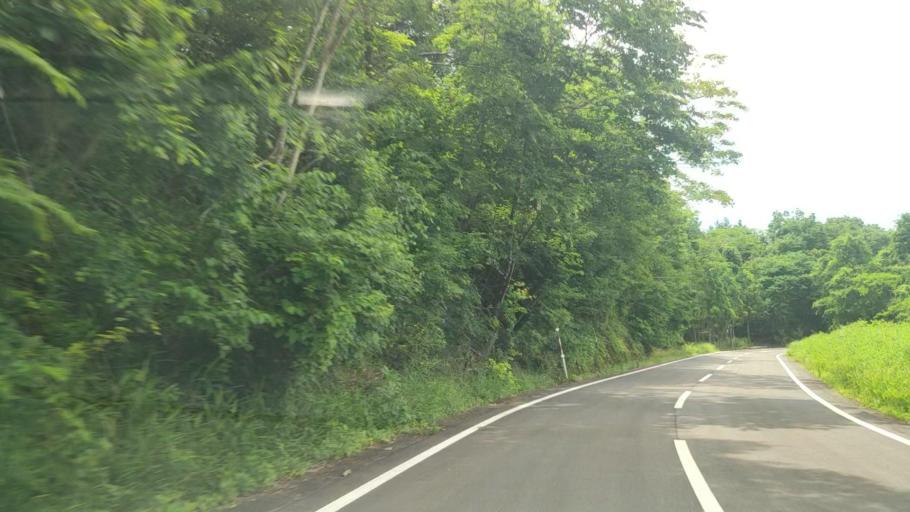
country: JP
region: Hyogo
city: Toyooka
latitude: 35.5106
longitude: 134.6856
